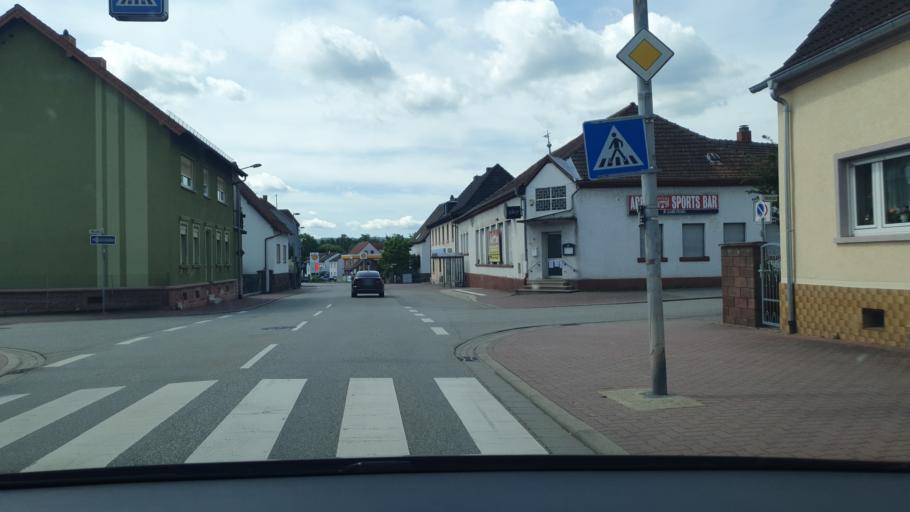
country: DE
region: Rheinland-Pfalz
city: Ramstein-Miesenbach
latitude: 49.4418
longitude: 7.5561
